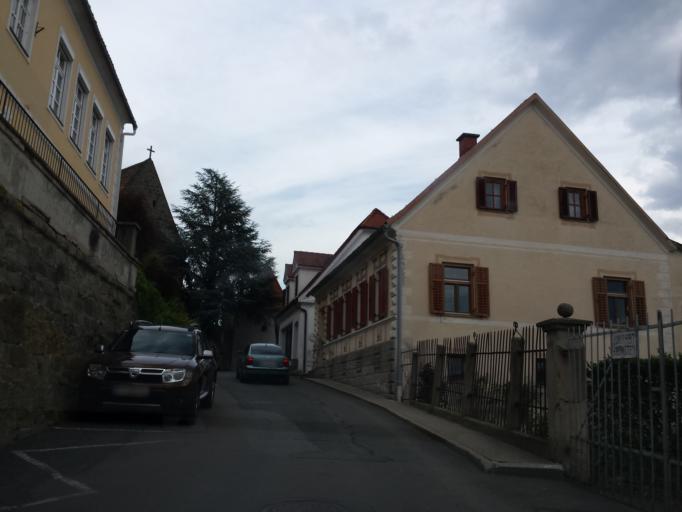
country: AT
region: Styria
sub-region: Politischer Bezirk Suedoststeiermark
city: Riegersburg
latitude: 47.0015
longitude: 15.9333
